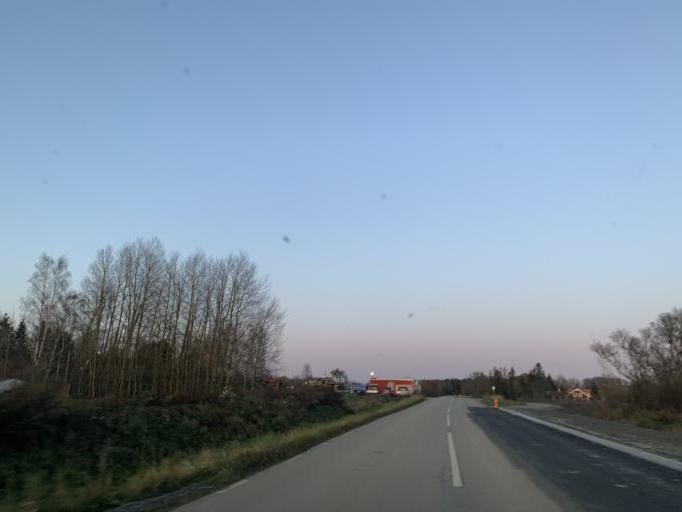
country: SE
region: OErebro
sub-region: Lindesbergs Kommun
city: Frovi
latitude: 59.3116
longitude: 15.3677
